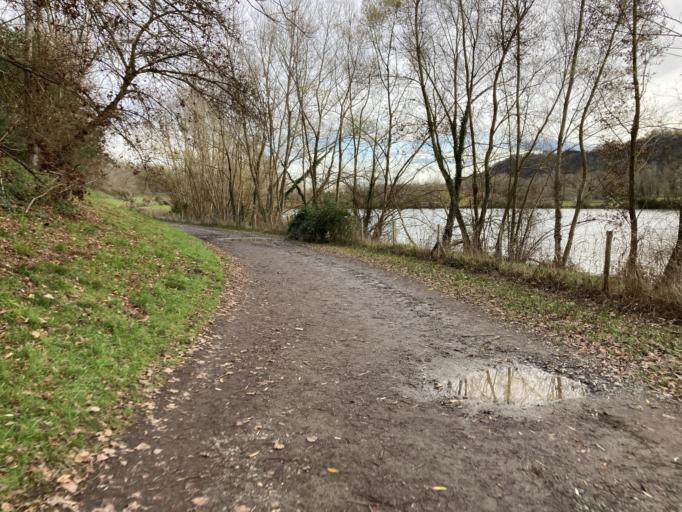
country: FR
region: Aquitaine
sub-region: Departement des Pyrenees-Atlantiques
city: Artiguelouve
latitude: 43.3107
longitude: -0.4416
